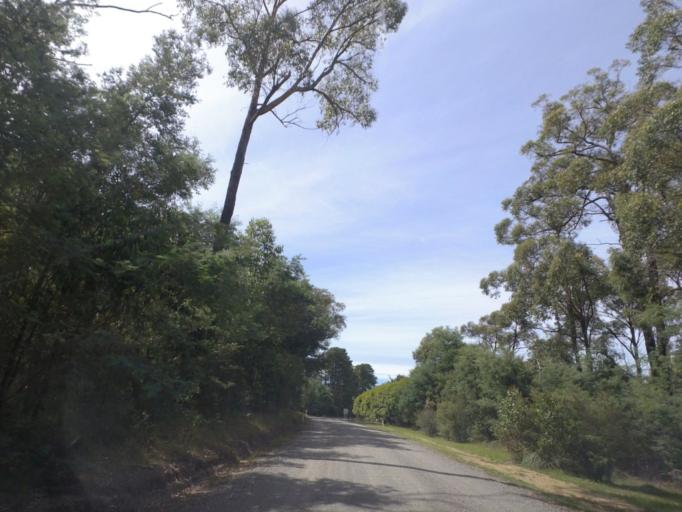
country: AU
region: Victoria
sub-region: Yarra Ranges
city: Yarra Glen
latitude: -37.5205
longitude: 145.4307
